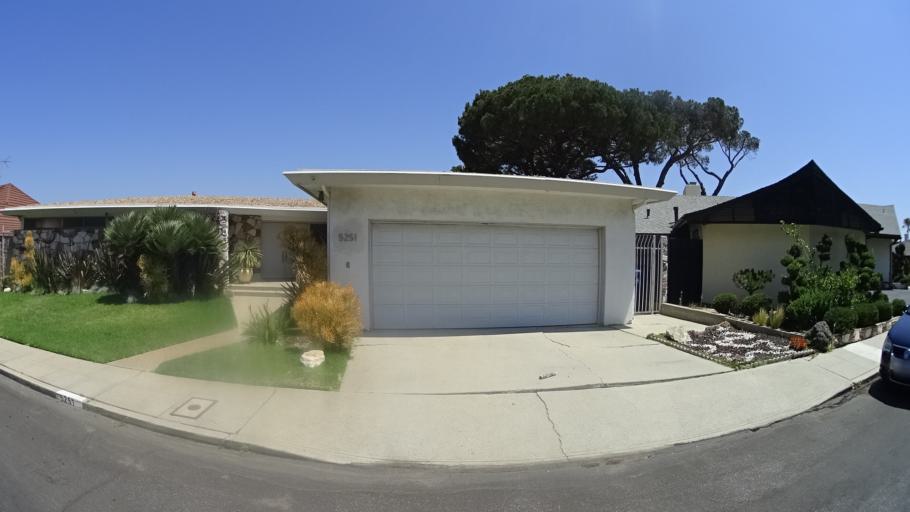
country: US
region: California
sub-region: Los Angeles County
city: View Park-Windsor Hills
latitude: 34.0124
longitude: -118.3594
